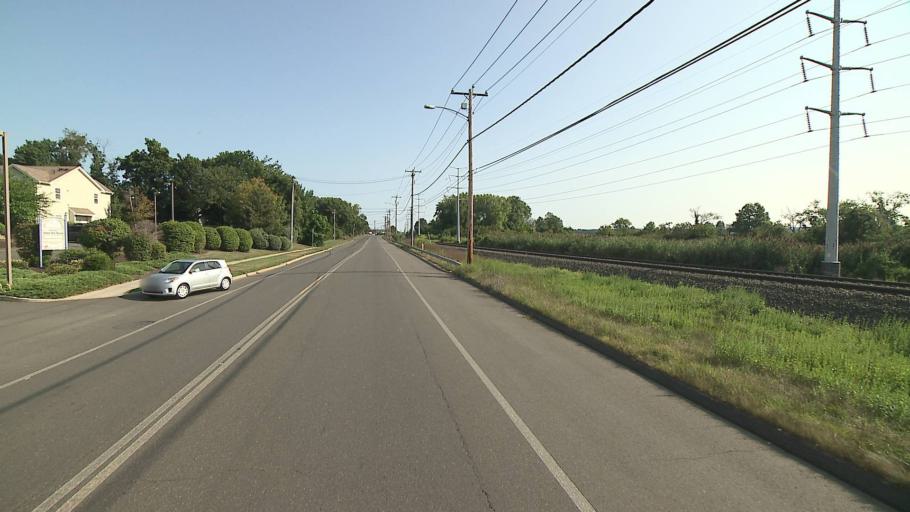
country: US
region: Connecticut
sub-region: New Haven County
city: New Haven
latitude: 41.3452
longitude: -72.8946
